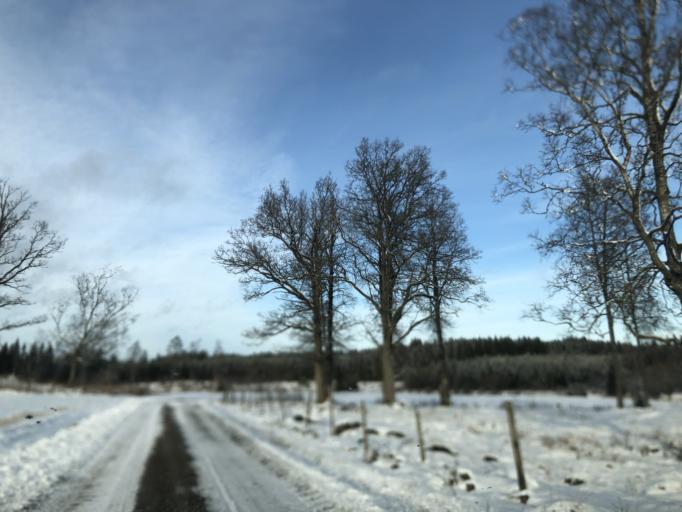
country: SE
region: Vaestra Goetaland
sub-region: Ulricehamns Kommun
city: Ulricehamn
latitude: 57.7371
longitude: 13.4924
